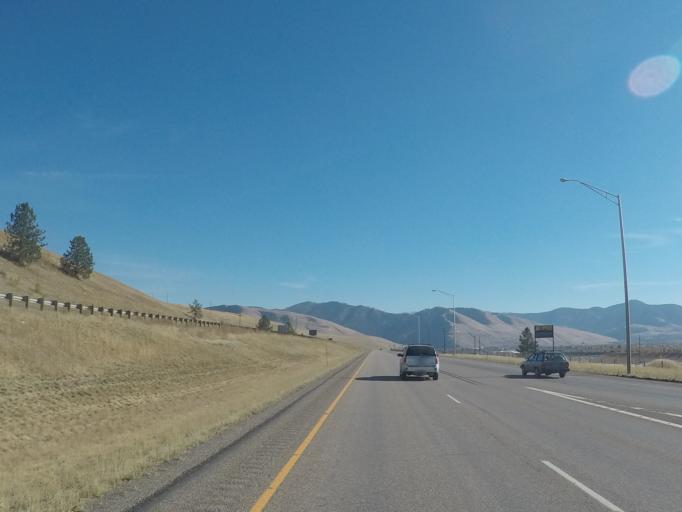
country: US
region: Montana
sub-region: Missoula County
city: Orchard Homes
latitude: 46.9105
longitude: -114.0305
